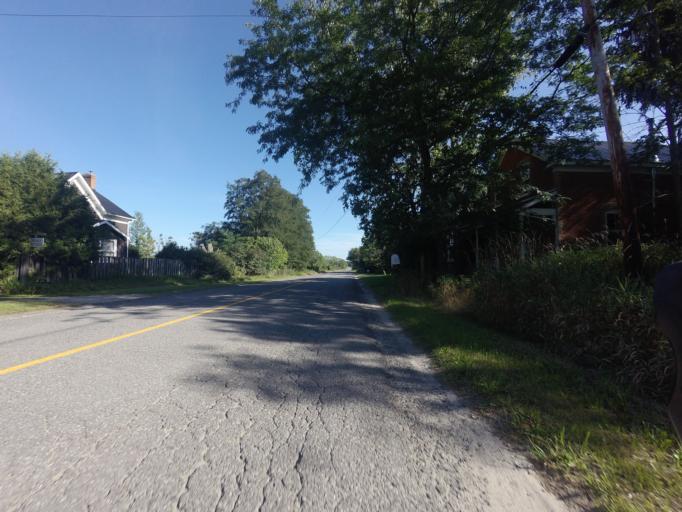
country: CA
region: Ontario
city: Perth
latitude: 44.9184
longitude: -76.3545
